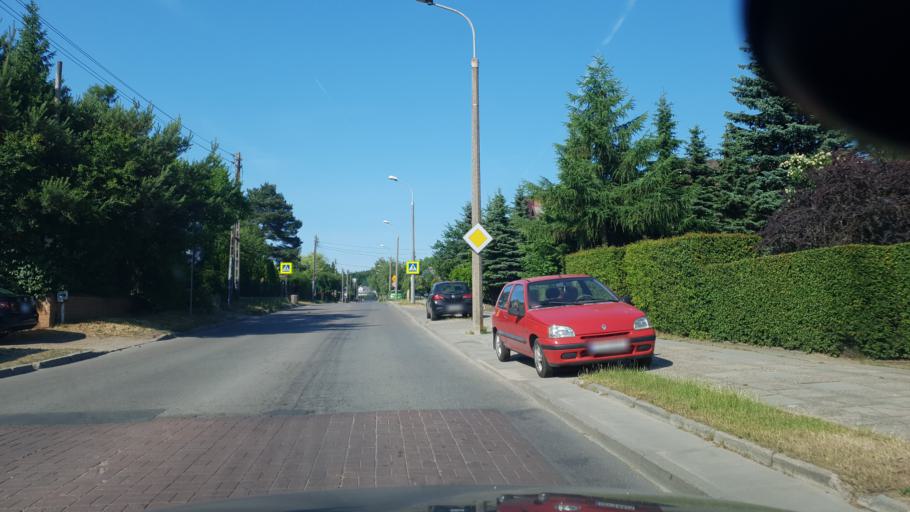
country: PL
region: Pomeranian Voivodeship
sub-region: Gdynia
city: Wielki Kack
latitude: 54.4322
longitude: 18.4641
